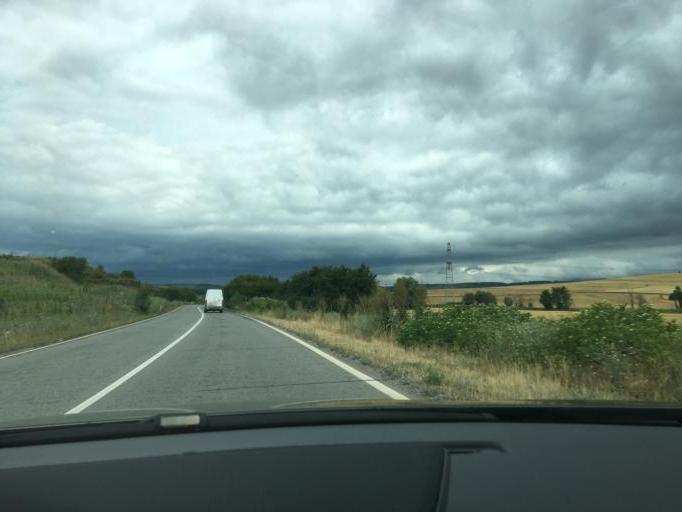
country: BG
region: Kyustendil
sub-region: Obshtina Dupnitsa
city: Dupnitsa
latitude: 42.2732
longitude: 23.0237
